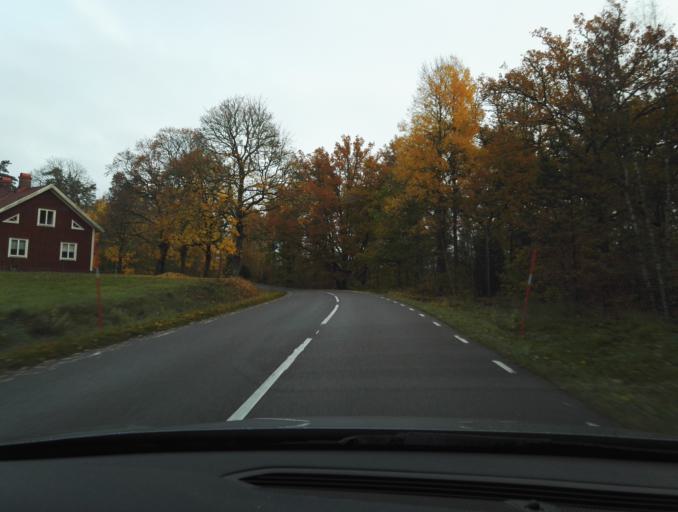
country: SE
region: Kronoberg
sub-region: Vaxjo Kommun
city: Rottne
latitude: 57.0100
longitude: 14.7731
